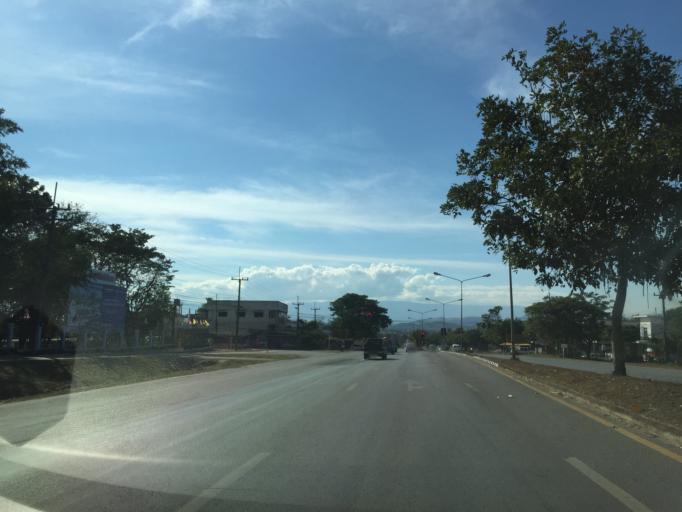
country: TH
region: Loei
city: Wang Saphung
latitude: 17.3017
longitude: 101.7900
